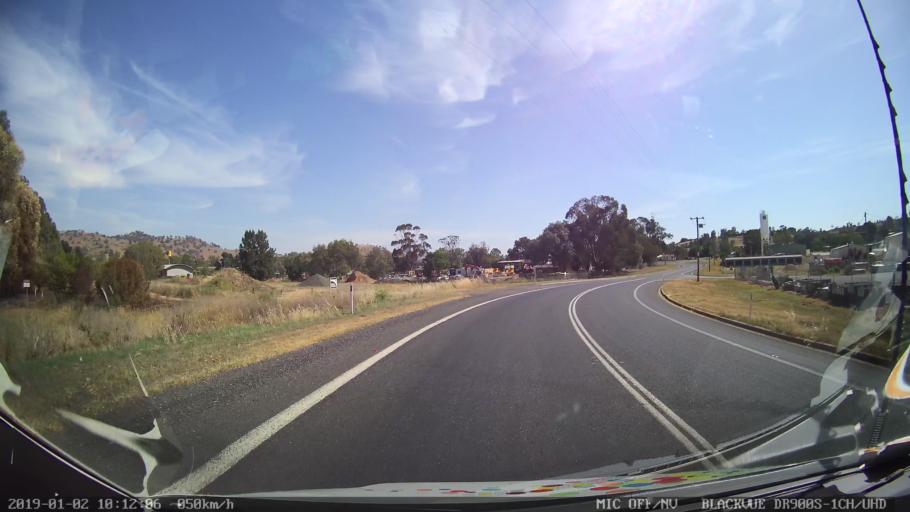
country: AU
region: New South Wales
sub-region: Gundagai
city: Gundagai
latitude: -35.0869
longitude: 148.0940
